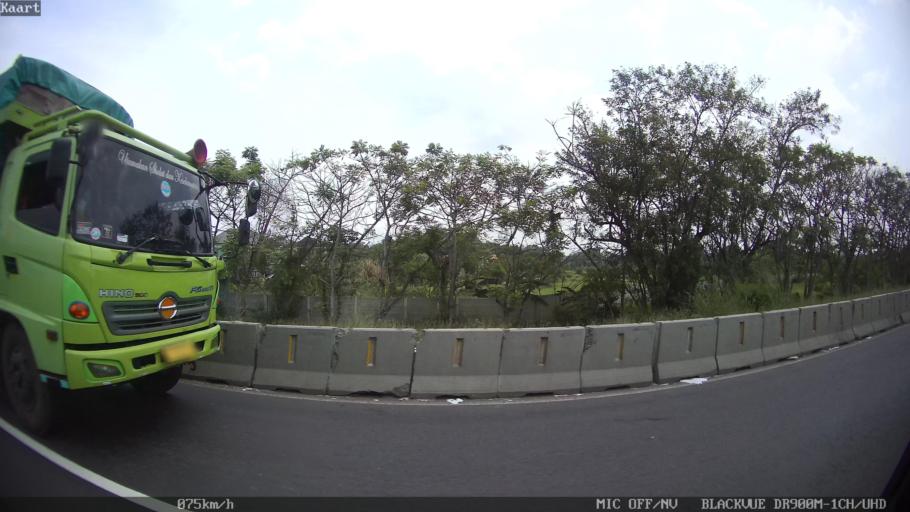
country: ID
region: Banten
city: Serang
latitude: -6.1182
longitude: 106.1881
